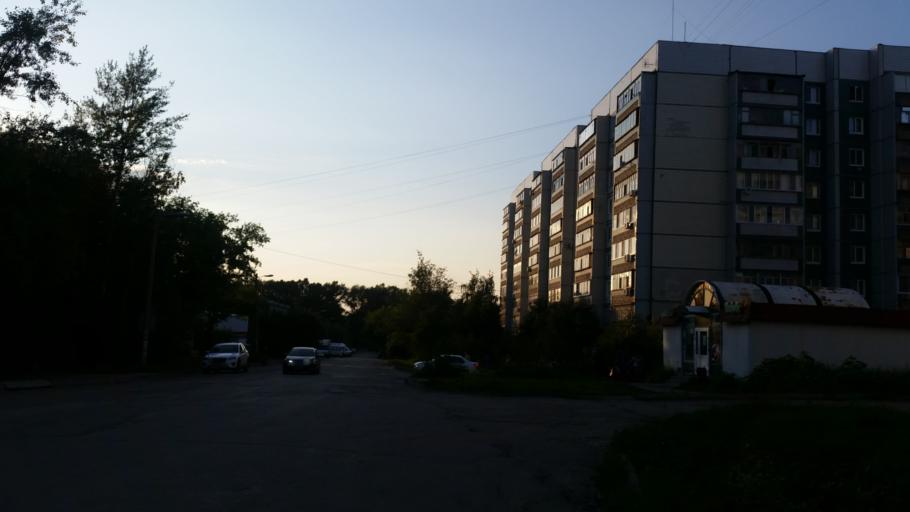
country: RU
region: Ulyanovsk
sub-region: Ulyanovskiy Rayon
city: Ulyanovsk
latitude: 54.3571
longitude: 48.3830
